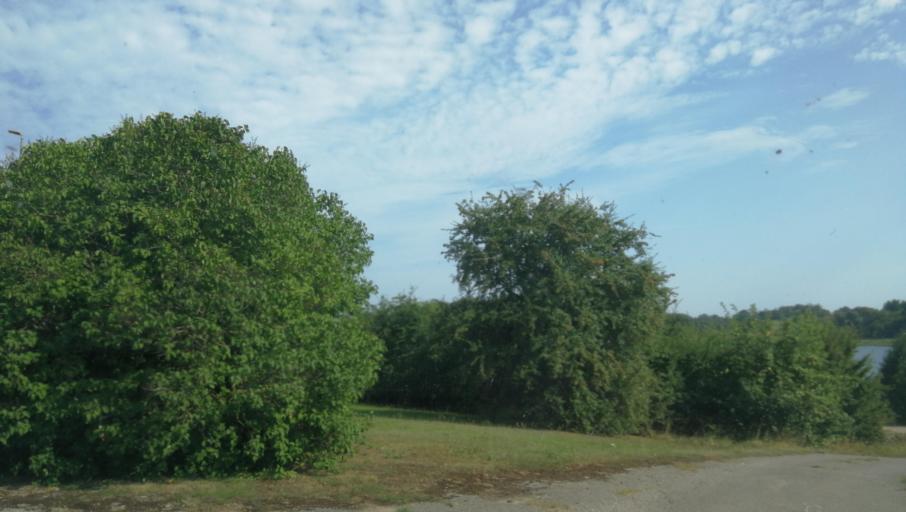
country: LV
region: Aizpute
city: Aizpute
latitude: 56.7103
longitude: 21.6271
